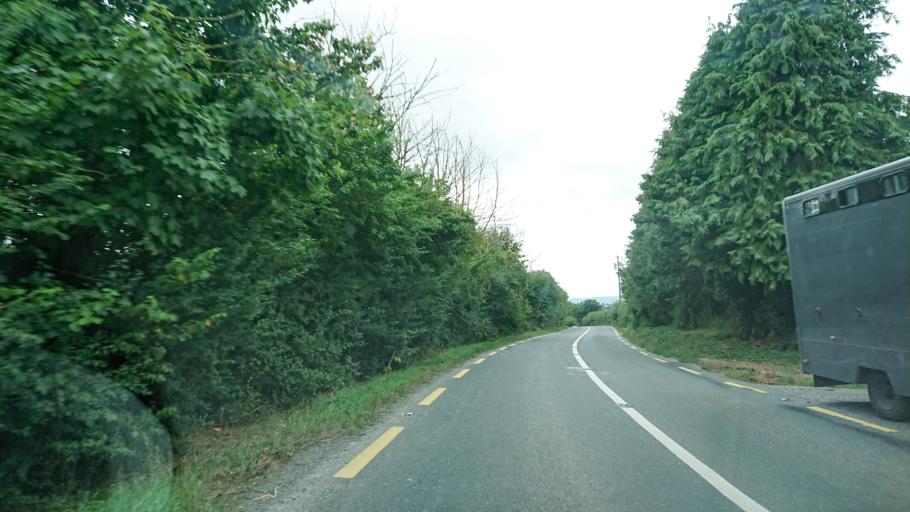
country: IE
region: Munster
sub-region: County Cork
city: Mallow
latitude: 52.1514
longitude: -8.5997
